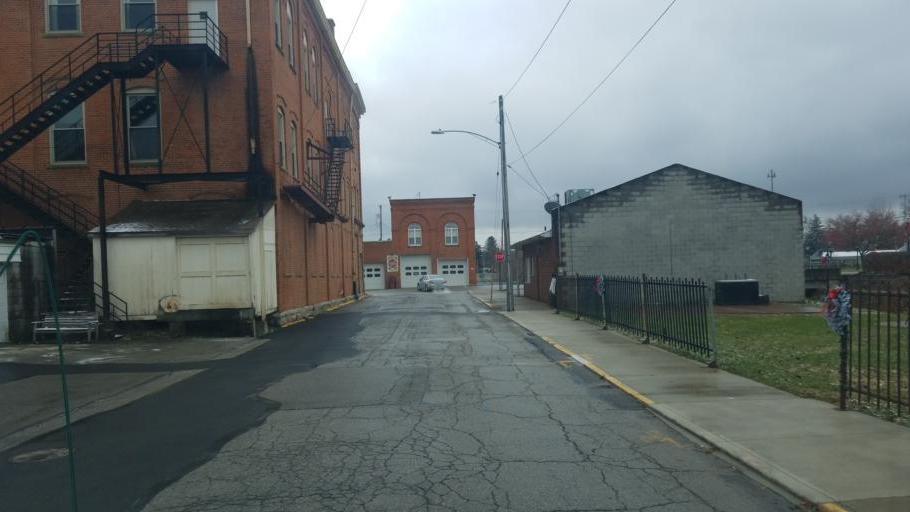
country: US
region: Ohio
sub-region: Richland County
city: Shelby
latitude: 40.8819
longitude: -82.6591
